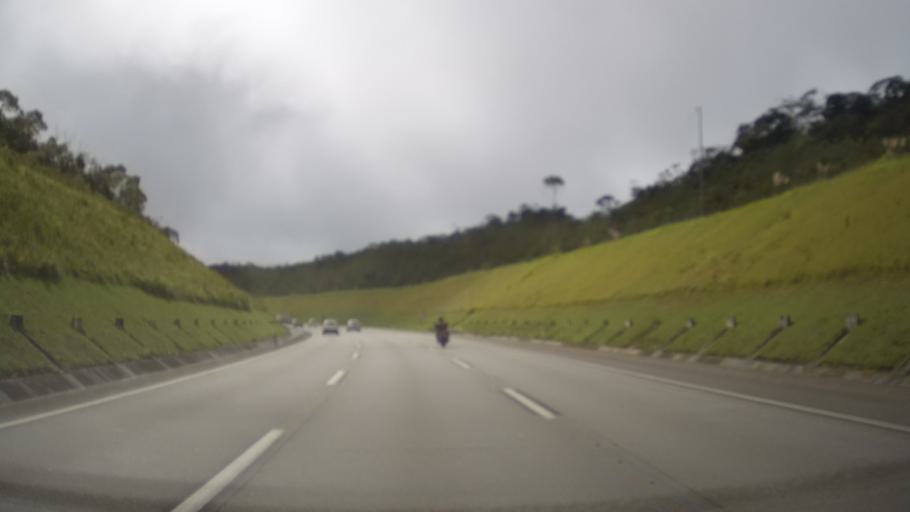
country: BR
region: Sao Paulo
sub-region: Cubatao
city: Cubatao
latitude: -23.9284
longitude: -46.5521
